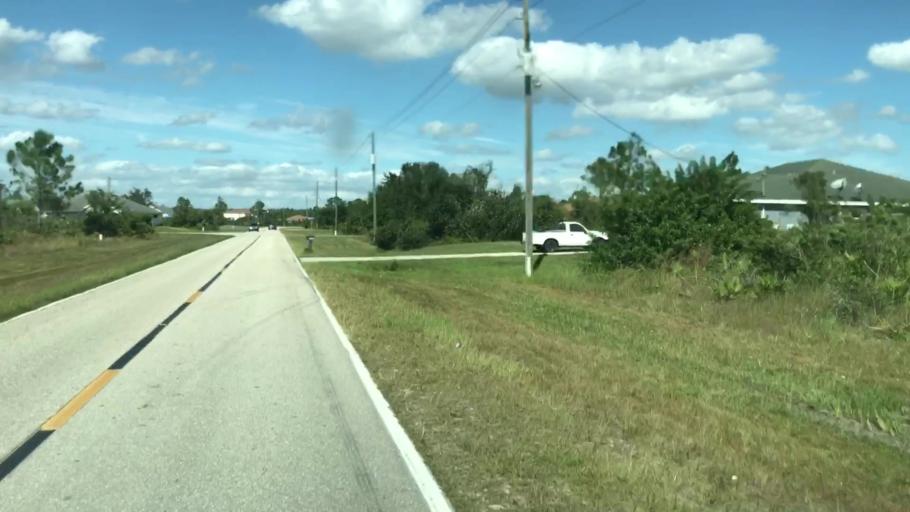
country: US
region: Florida
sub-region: Lee County
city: Lehigh Acres
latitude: 26.6708
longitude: -81.6258
